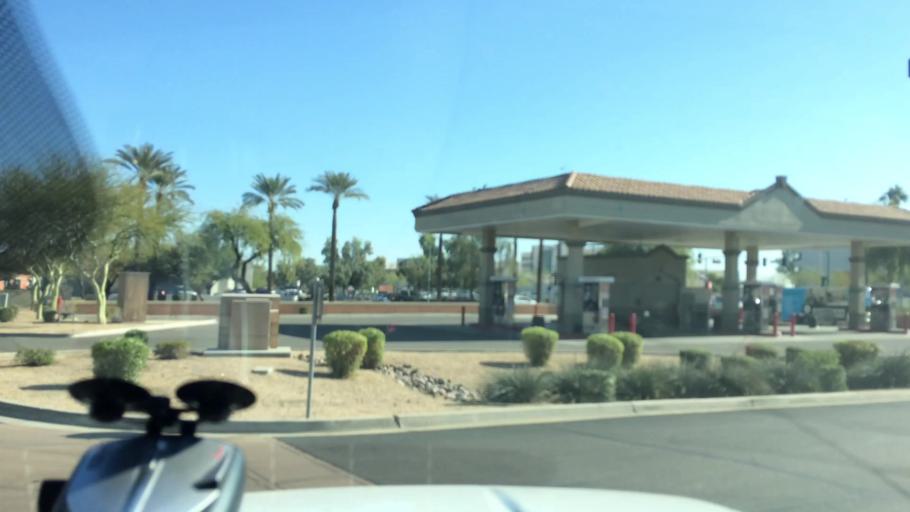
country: US
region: Arizona
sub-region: Maricopa County
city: Peoria
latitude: 33.6115
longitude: -112.1841
